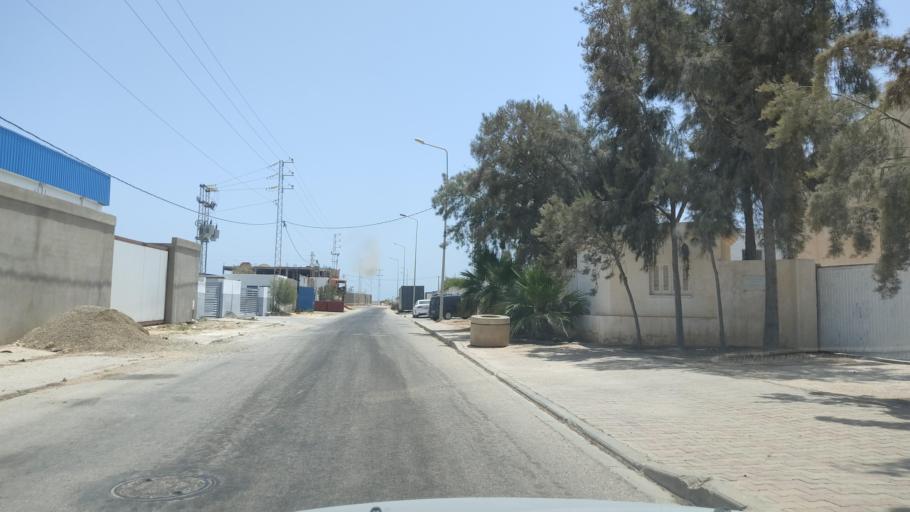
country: TN
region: Safaqis
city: Sfax
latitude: 34.6616
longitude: 10.6983
